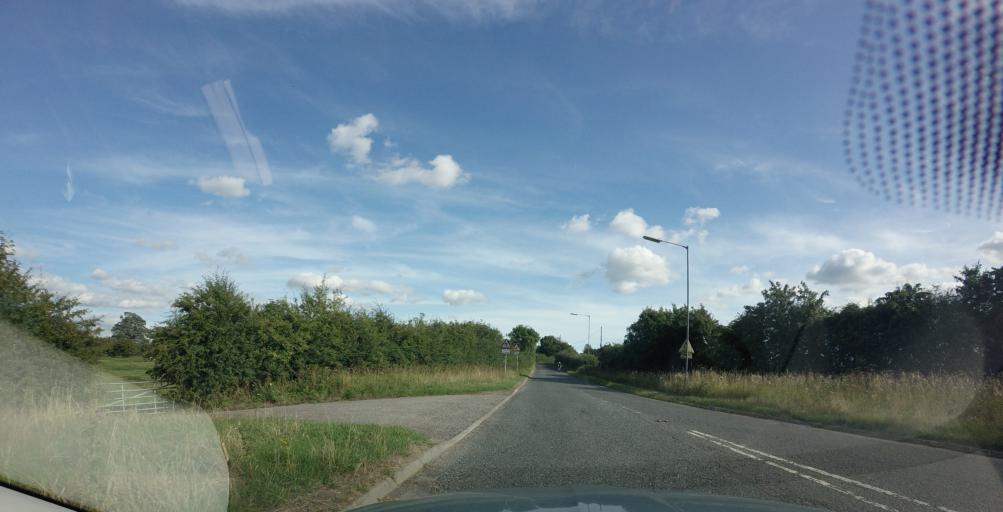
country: GB
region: England
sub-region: North Yorkshire
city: Ripon
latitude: 54.1234
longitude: -1.5187
